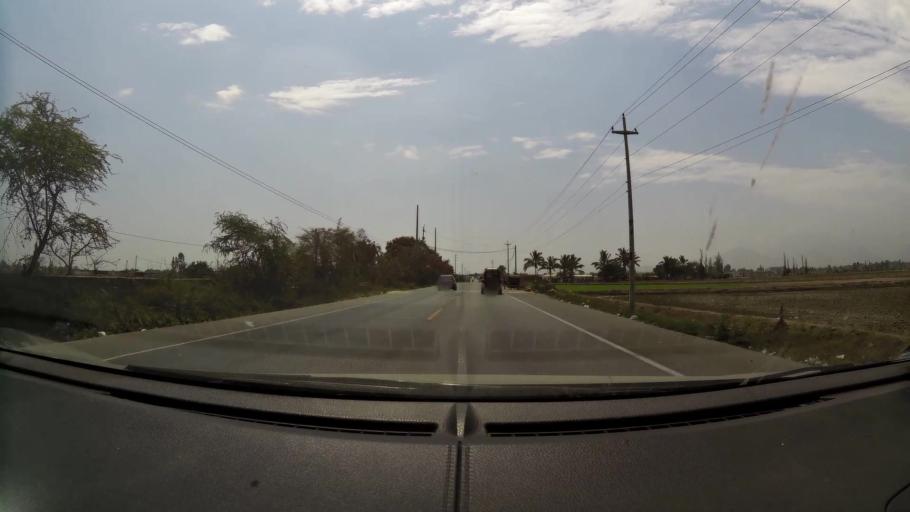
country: PE
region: La Libertad
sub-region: Chepen
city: Pacanga
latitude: -7.1660
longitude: -79.4407
